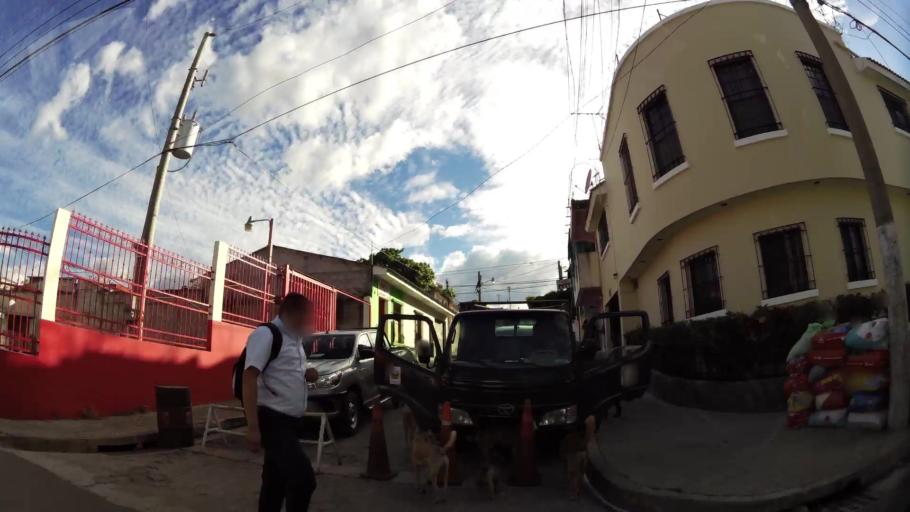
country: SV
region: Cuscatlan
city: Cojutepeque
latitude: 13.7226
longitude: -88.9371
